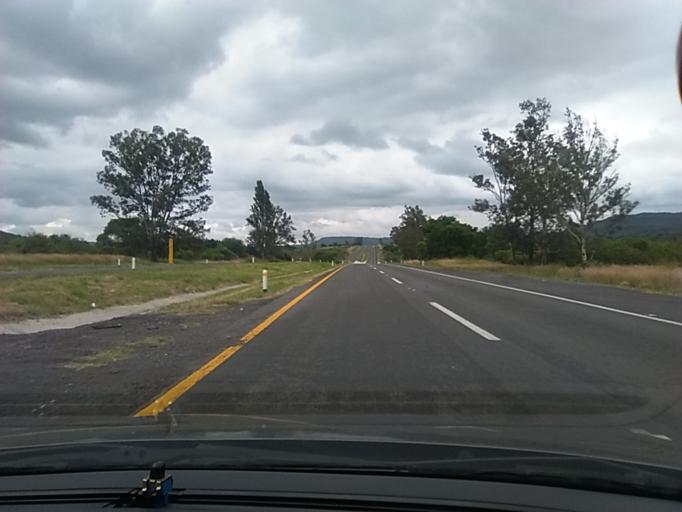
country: MX
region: Jalisco
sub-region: Zapotlanejo
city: La Mezquitera
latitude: 20.5525
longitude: -103.0496
